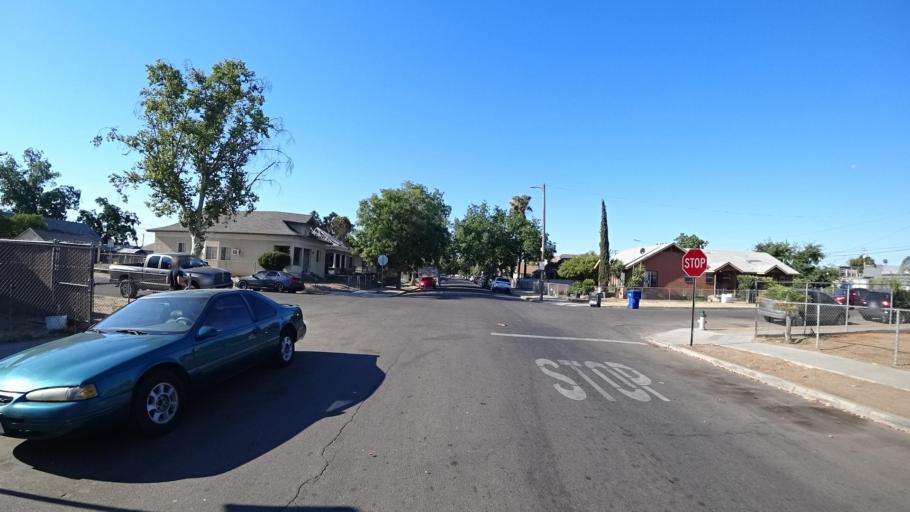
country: US
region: California
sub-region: Fresno County
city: Fresno
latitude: 36.7488
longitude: -119.7883
